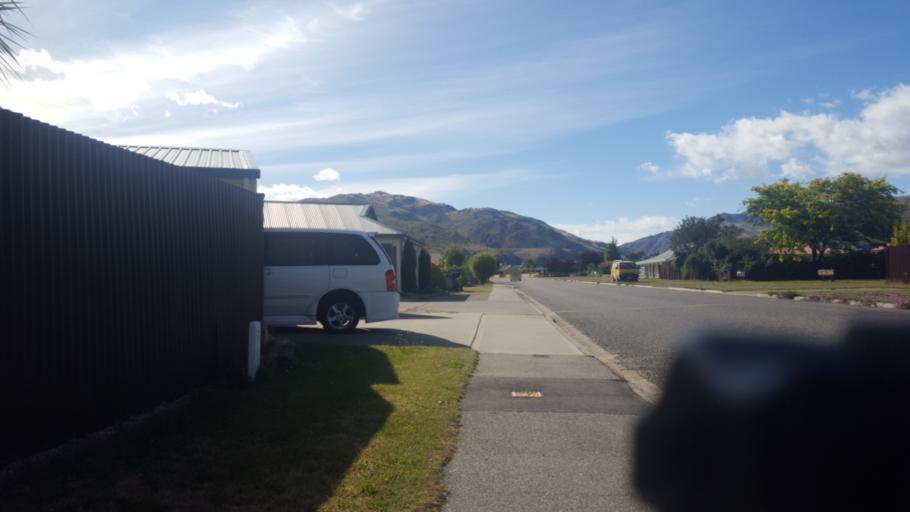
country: NZ
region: Otago
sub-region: Queenstown-Lakes District
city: Wanaka
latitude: -45.0470
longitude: 169.1980
